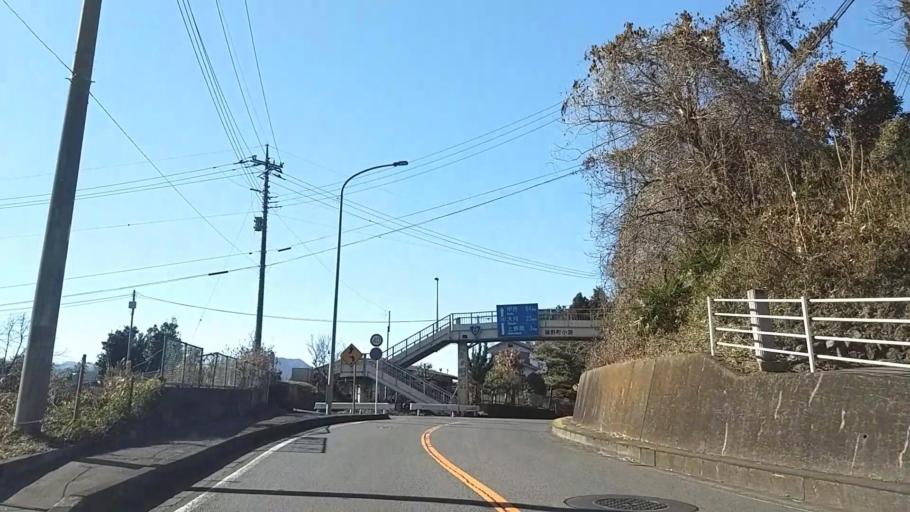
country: JP
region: Yamanashi
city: Uenohara
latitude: 35.6193
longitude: 139.1400
